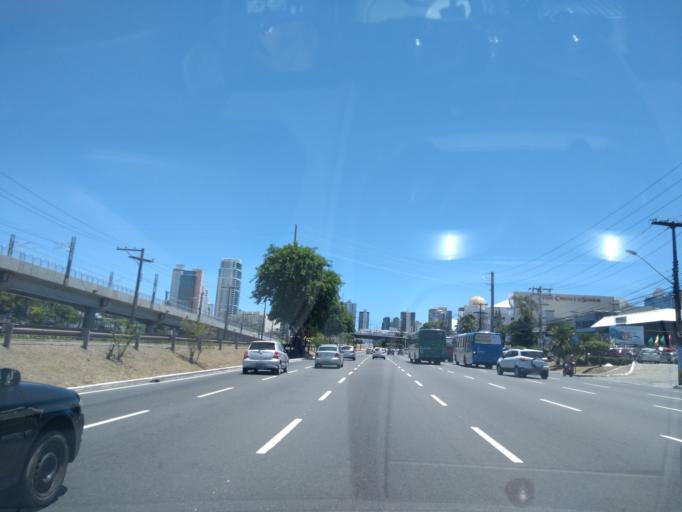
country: BR
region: Bahia
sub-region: Salvador
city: Salvador
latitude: -12.9790
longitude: -38.4697
